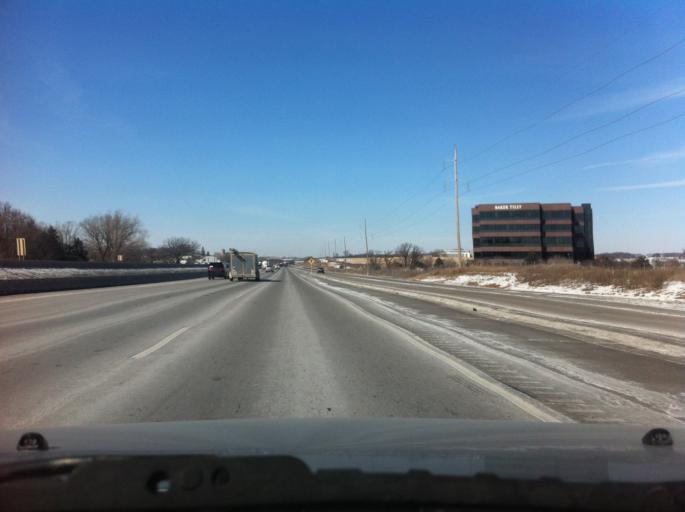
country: US
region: Wisconsin
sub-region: Dane County
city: Monona
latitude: 43.1272
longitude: -89.2912
